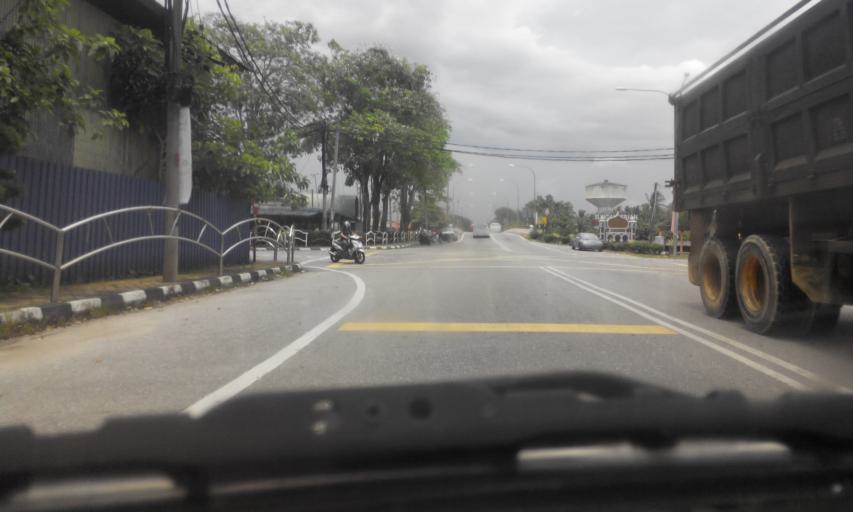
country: MY
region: Perak
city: Parit Buntar
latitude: 5.1282
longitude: 100.4938
